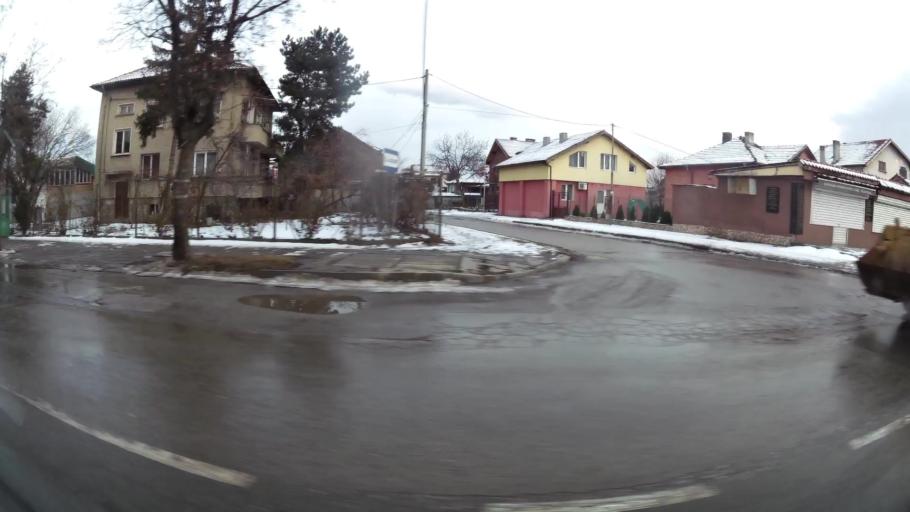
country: BG
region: Sofia-Capital
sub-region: Stolichna Obshtina
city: Sofia
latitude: 42.7241
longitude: 23.3437
